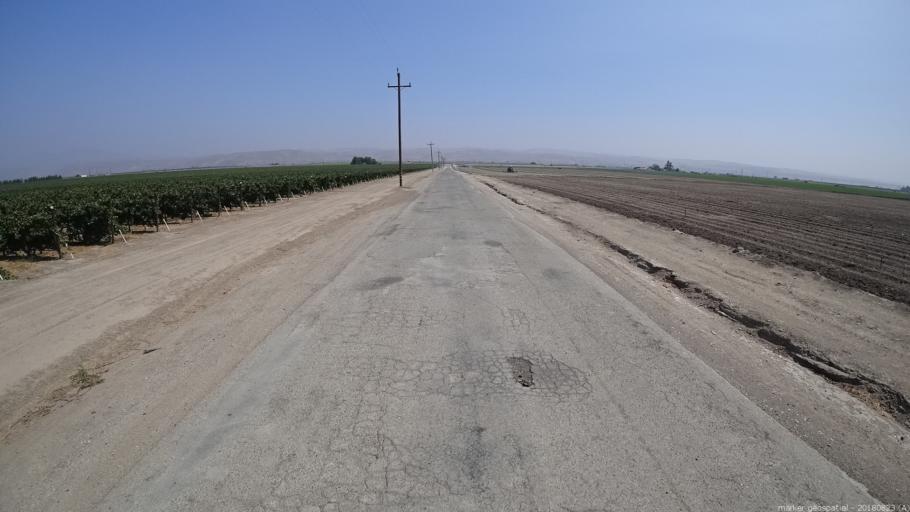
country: US
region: California
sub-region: Monterey County
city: Greenfield
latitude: 36.2844
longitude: -121.2017
